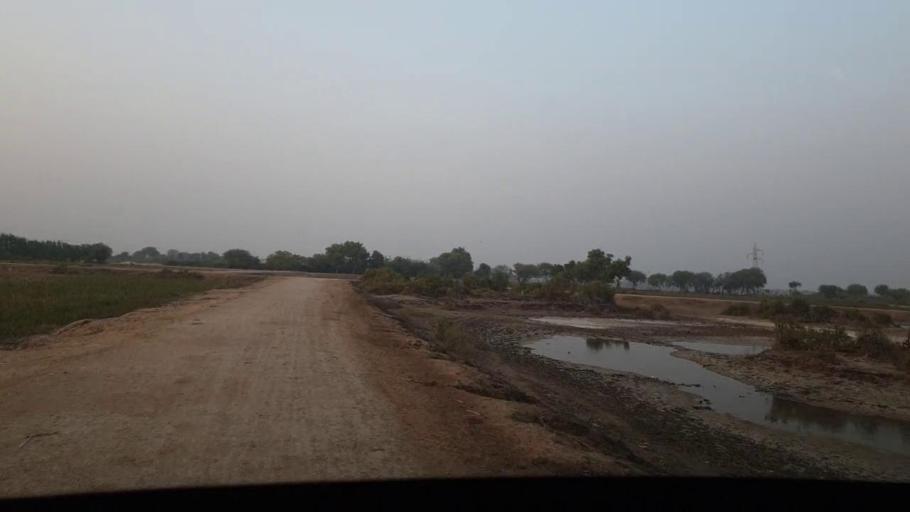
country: PK
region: Sindh
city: Chuhar Jamali
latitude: 24.4628
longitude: 68.0324
